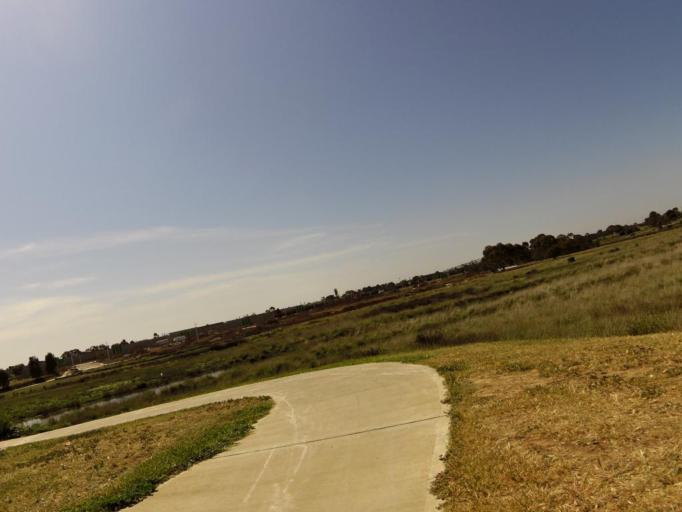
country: AU
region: Victoria
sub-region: Wyndham
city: Williams Landing
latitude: -37.8796
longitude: 144.7262
